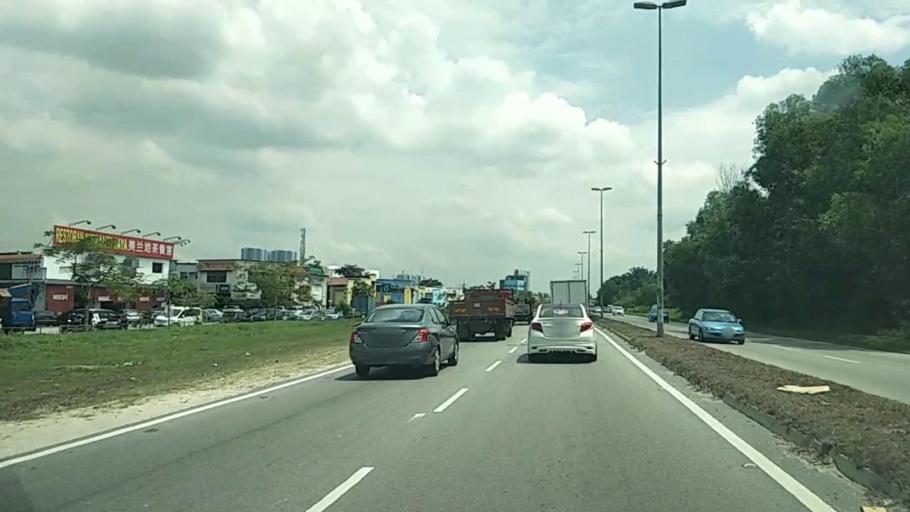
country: MY
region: Selangor
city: Subang Jaya
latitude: 2.9706
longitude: 101.6131
